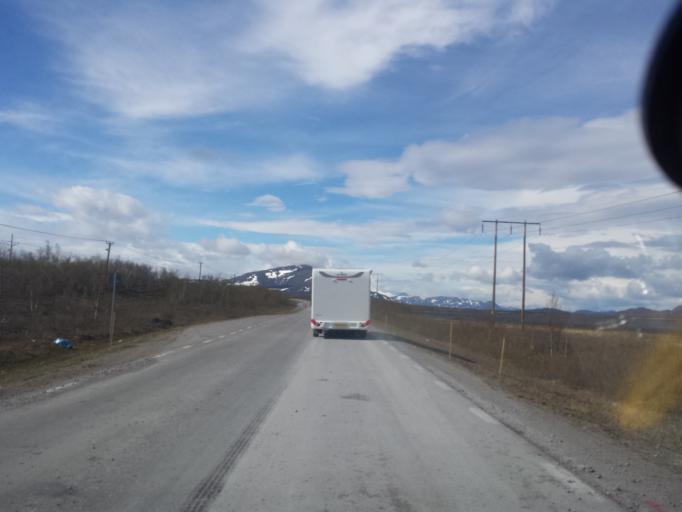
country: SE
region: Norrbotten
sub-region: Kiruna Kommun
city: Kiruna
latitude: 68.1104
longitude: 19.8351
